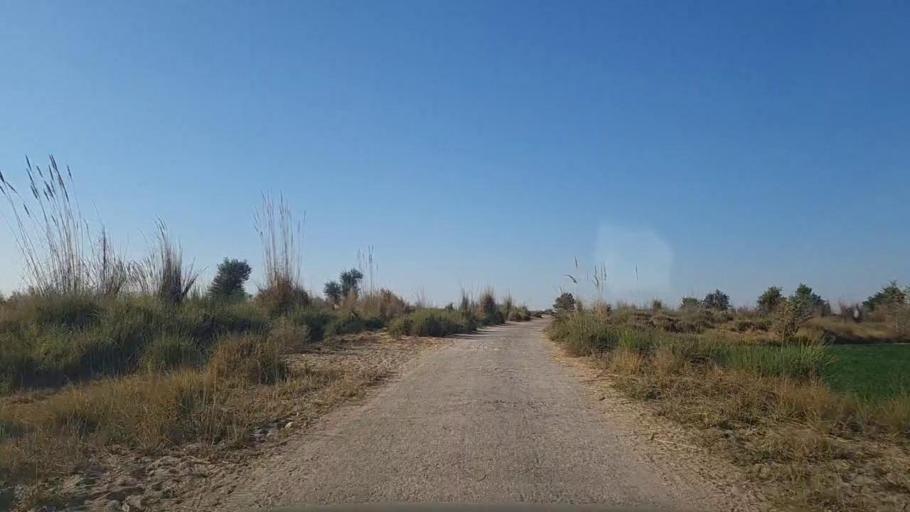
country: PK
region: Sindh
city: Khadro
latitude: 26.2424
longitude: 68.8640
